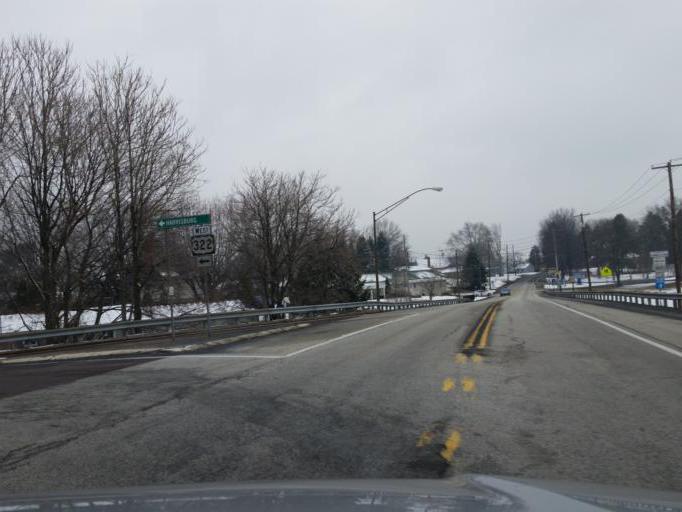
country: US
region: Pennsylvania
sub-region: Dauphin County
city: Hummelstown
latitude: 40.2584
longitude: -76.7090
